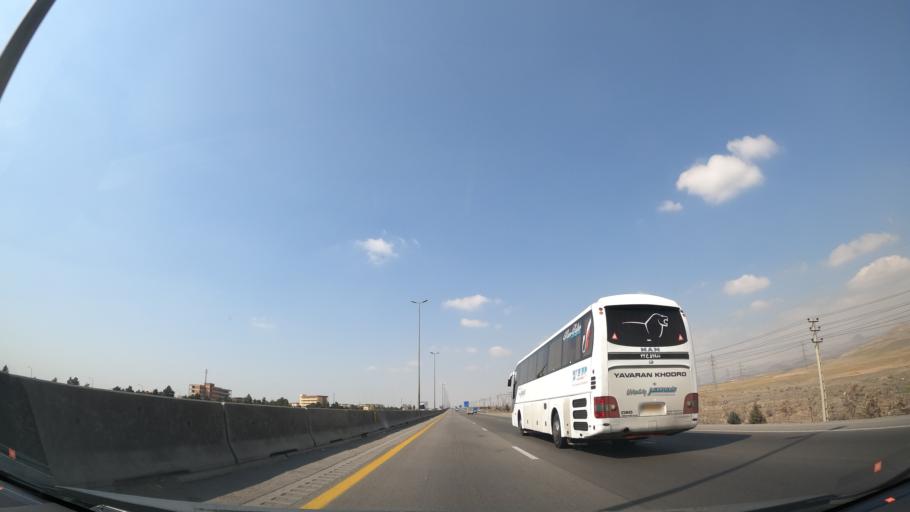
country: IR
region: Qazvin
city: Abyek
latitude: 36.0665
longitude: 50.4865
